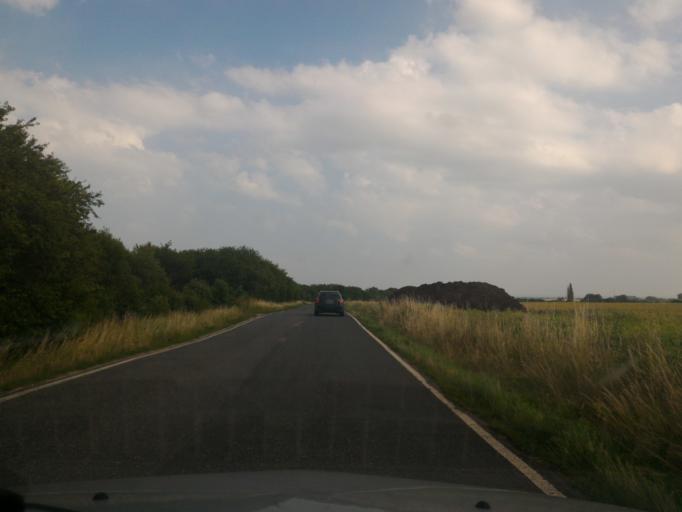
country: CZ
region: Central Bohemia
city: Loucen
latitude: 50.2624
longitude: 15.0225
